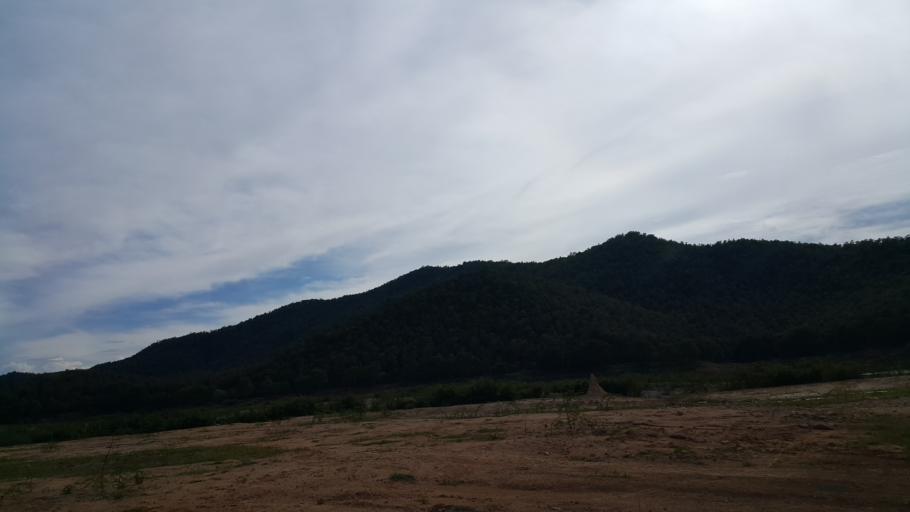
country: TH
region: Chiang Mai
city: Mae On
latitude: 18.7012
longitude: 99.2049
